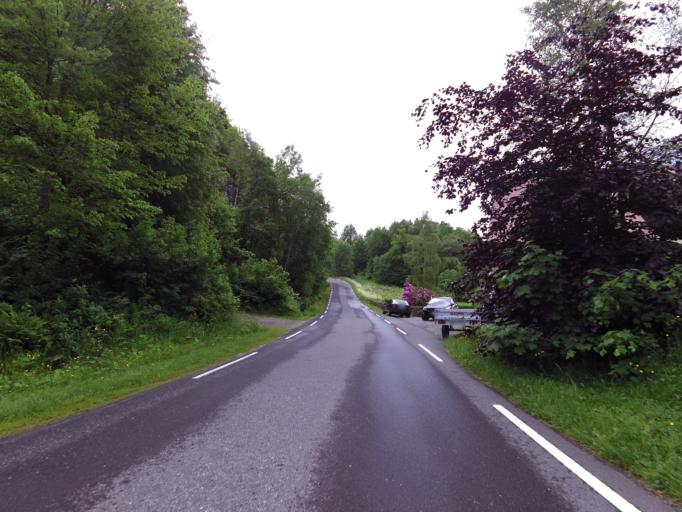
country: NO
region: Vest-Agder
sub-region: Lyngdal
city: Lyngdal
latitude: 58.1023
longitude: 6.9611
